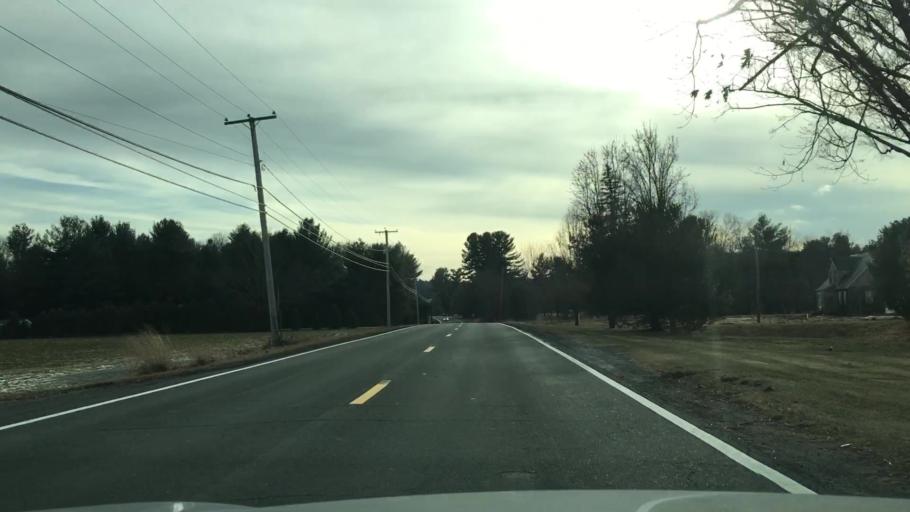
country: US
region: Massachusetts
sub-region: Hampden County
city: Southwick
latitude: 42.0848
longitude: -72.7658
